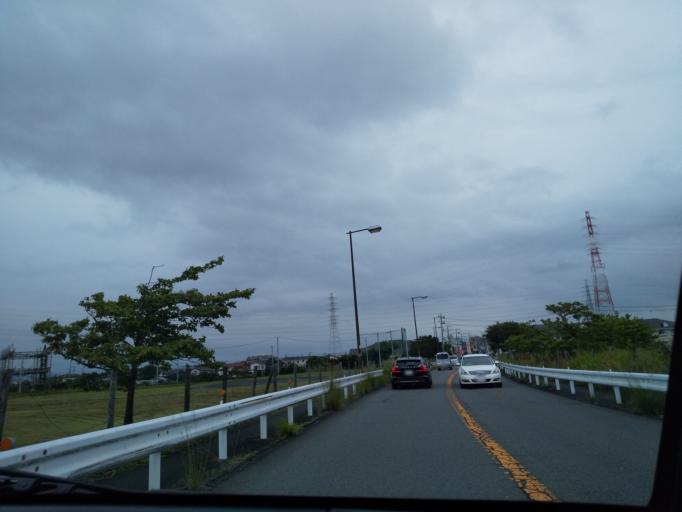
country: JP
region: Kanagawa
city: Fujisawa
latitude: 35.4010
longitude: 139.5020
